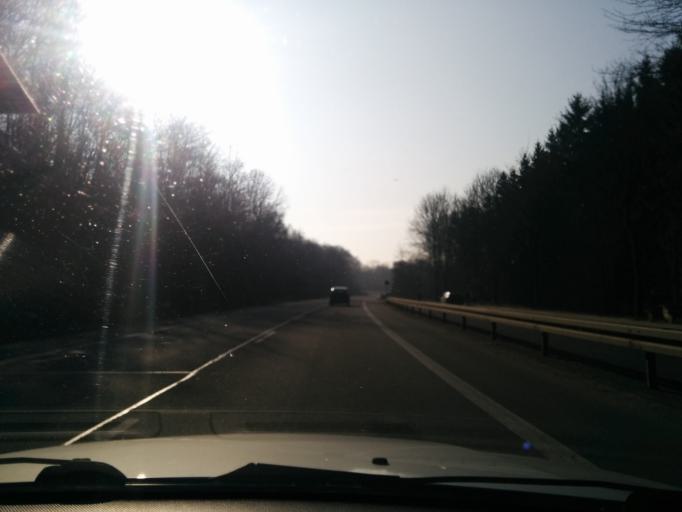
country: DE
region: North Rhine-Westphalia
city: Brakel
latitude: 51.6957
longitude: 9.1674
